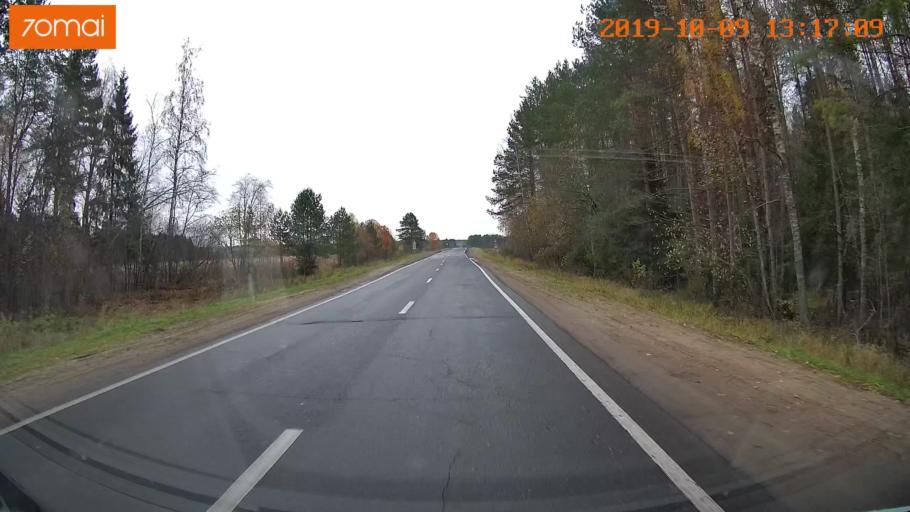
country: RU
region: Jaroslavl
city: Lyubim
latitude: 58.3561
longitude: 40.7760
